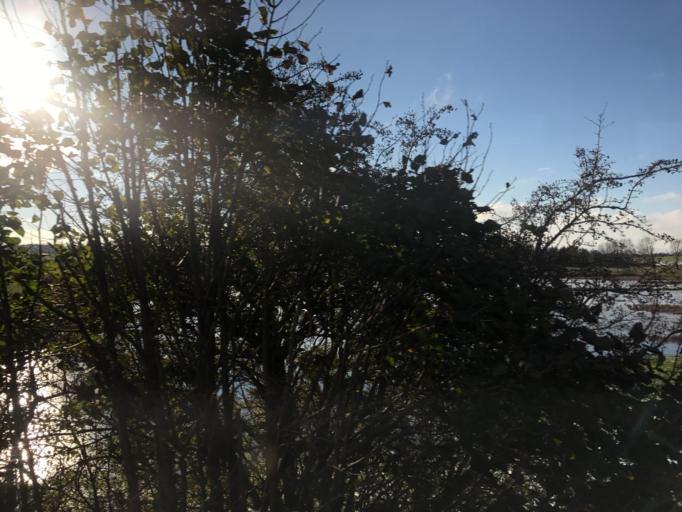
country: DK
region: Zealand
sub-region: Stevns Kommune
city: Harlev
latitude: 55.3538
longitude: 12.2640
